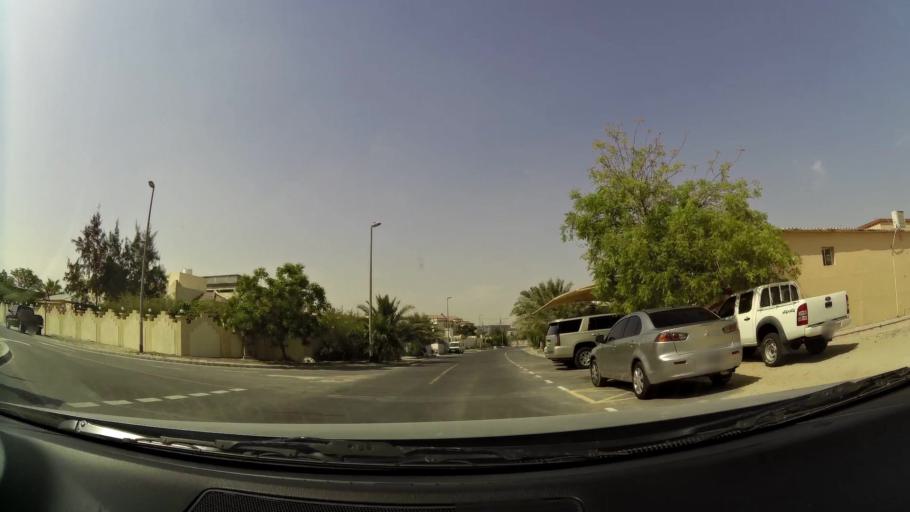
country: AE
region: Ash Shariqah
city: Sharjah
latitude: 25.2009
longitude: 55.3998
